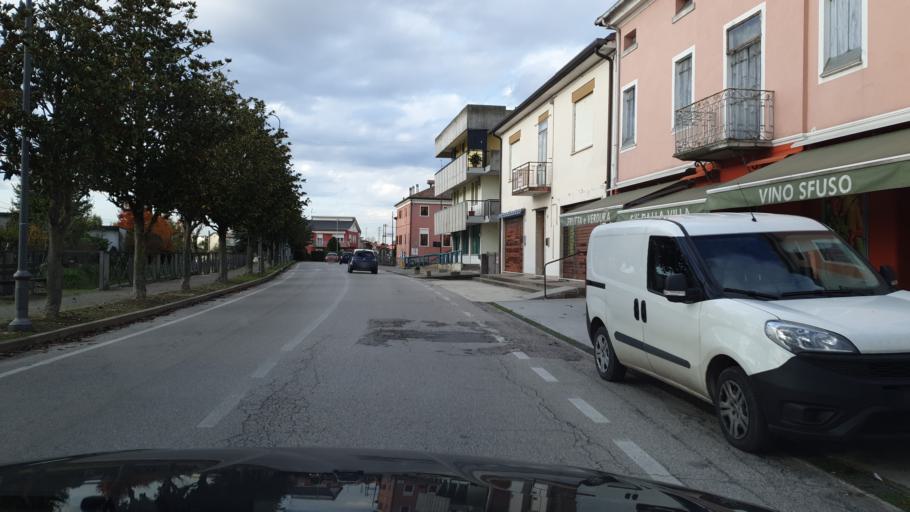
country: IT
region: Veneto
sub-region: Provincia di Rovigo
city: Villanova del Ghebbo Canton
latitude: 45.0565
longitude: 11.6438
